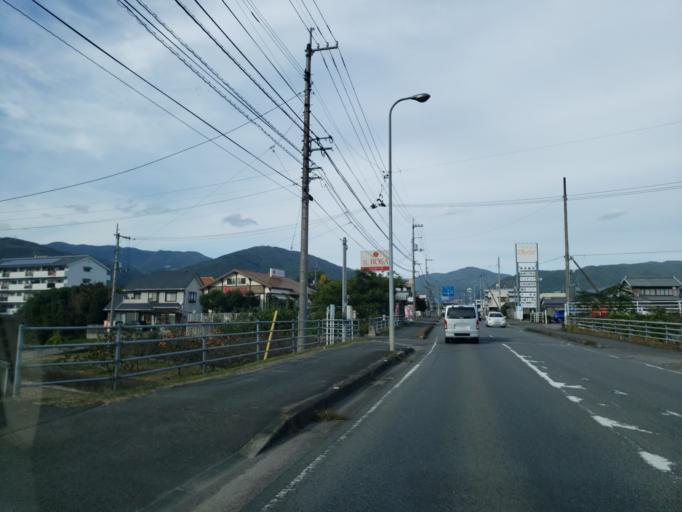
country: JP
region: Tokushima
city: Wakimachi
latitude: 34.0631
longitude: 134.1693
